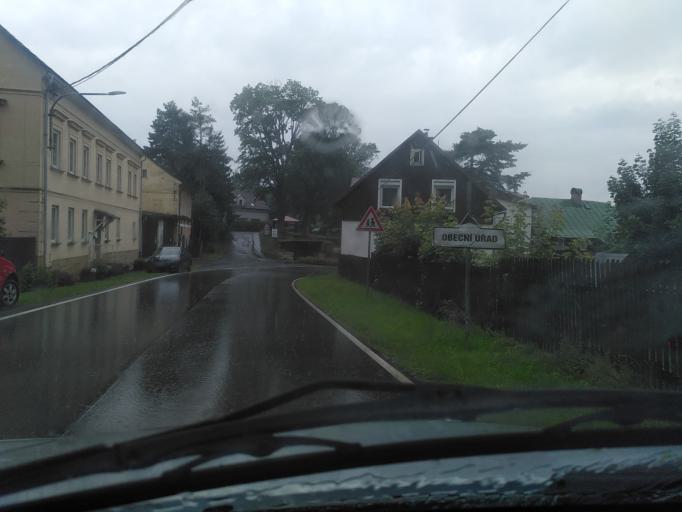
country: CZ
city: Novy Bor
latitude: 50.8121
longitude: 14.5363
